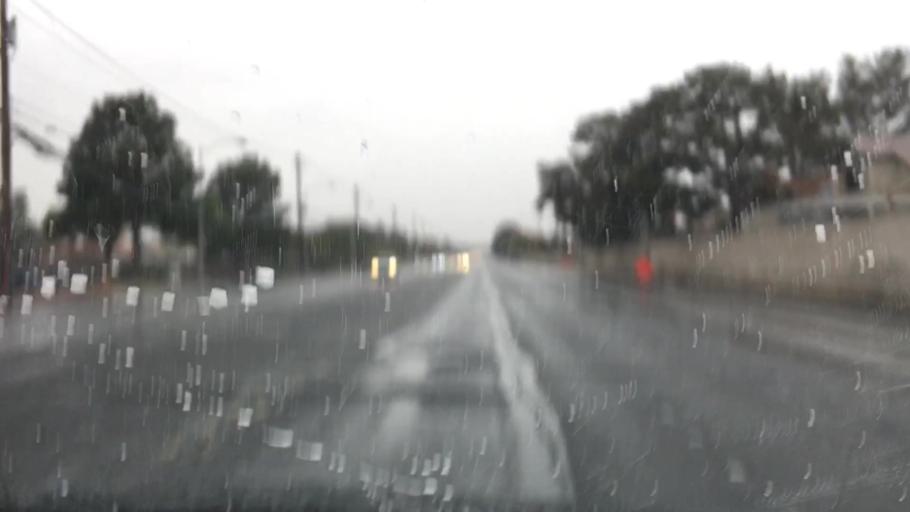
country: US
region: Nevada
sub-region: Clark County
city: Paradise
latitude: 36.0577
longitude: -115.1290
